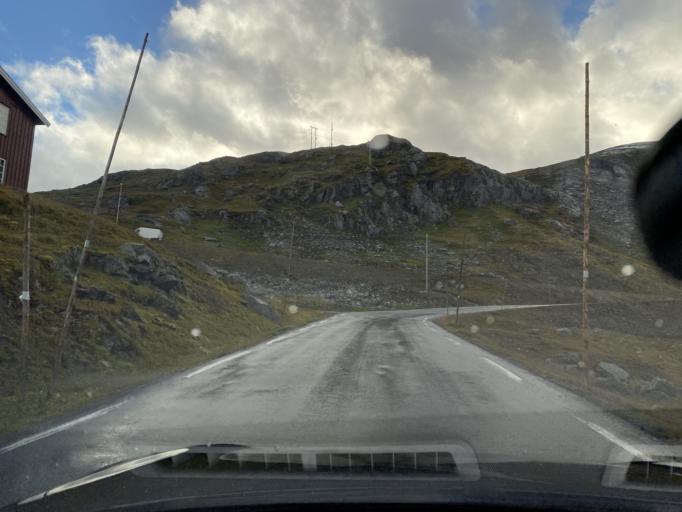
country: NO
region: Sogn og Fjordane
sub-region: Ardal
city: Farnes
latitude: 61.5745
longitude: 8.0329
